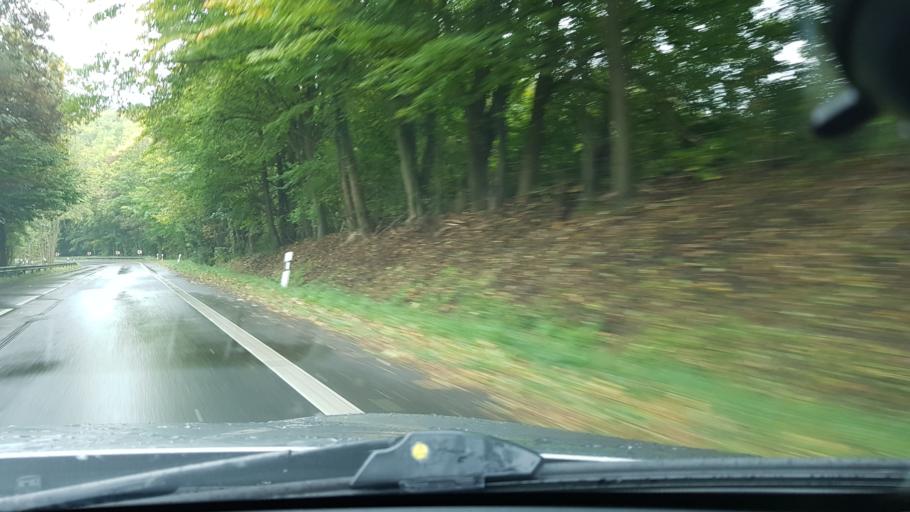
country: DE
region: Rheinland-Pfalz
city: Simmern
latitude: 50.3699
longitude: 7.6683
